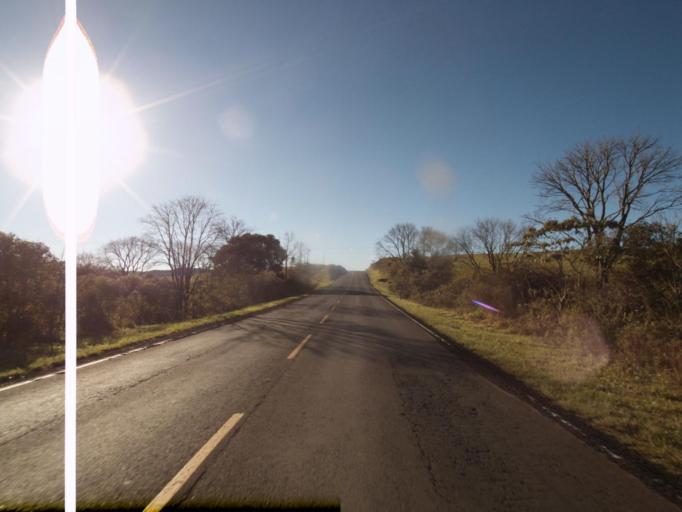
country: AR
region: Misiones
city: Bernardo de Irigoyen
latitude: -26.3531
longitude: -53.5440
